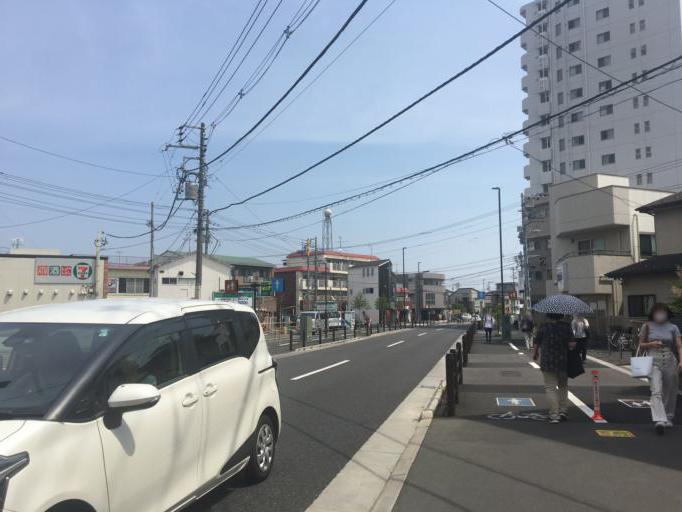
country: JP
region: Tokyo
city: Tanashicho
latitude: 35.7530
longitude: 139.5463
